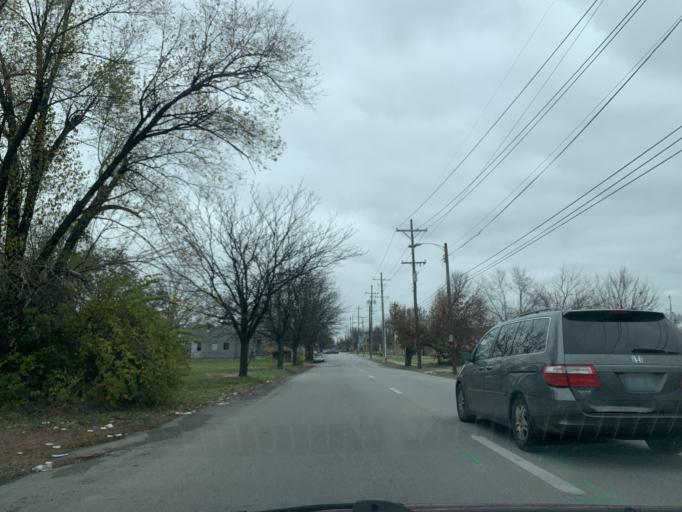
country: US
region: Kentucky
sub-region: Jefferson County
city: Louisville
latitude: 38.2474
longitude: -85.7869
